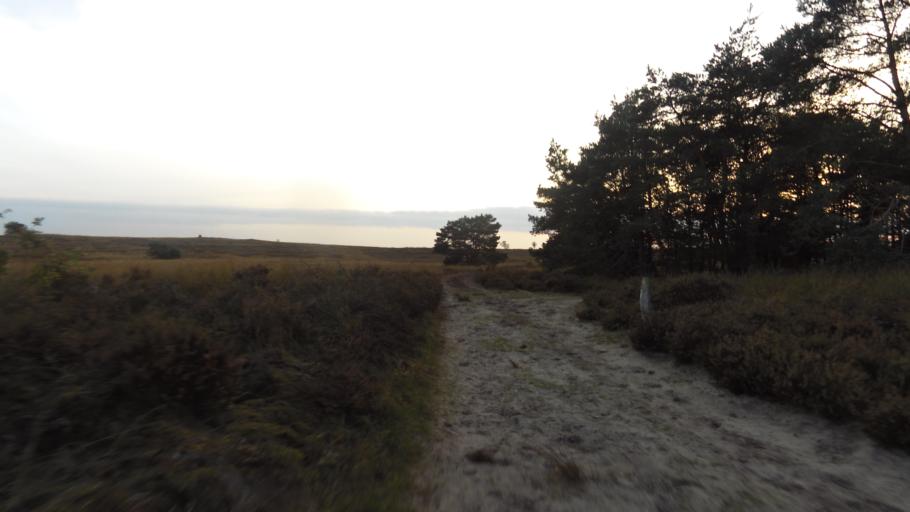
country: NL
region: Gelderland
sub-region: Gemeente Nunspeet
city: Nunspeet
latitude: 52.3269
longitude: 5.8016
